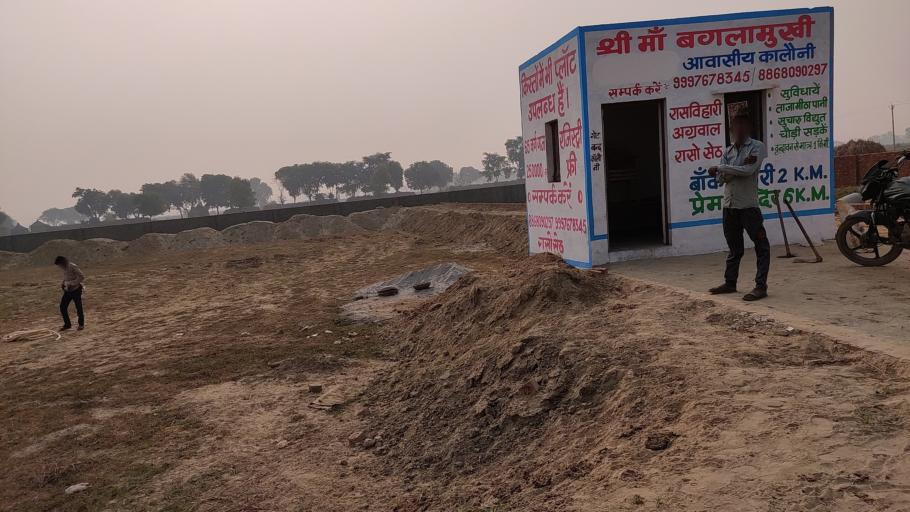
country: IN
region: Uttar Pradesh
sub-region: Mathura
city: Vrindavan
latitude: 27.5528
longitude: 77.7138
